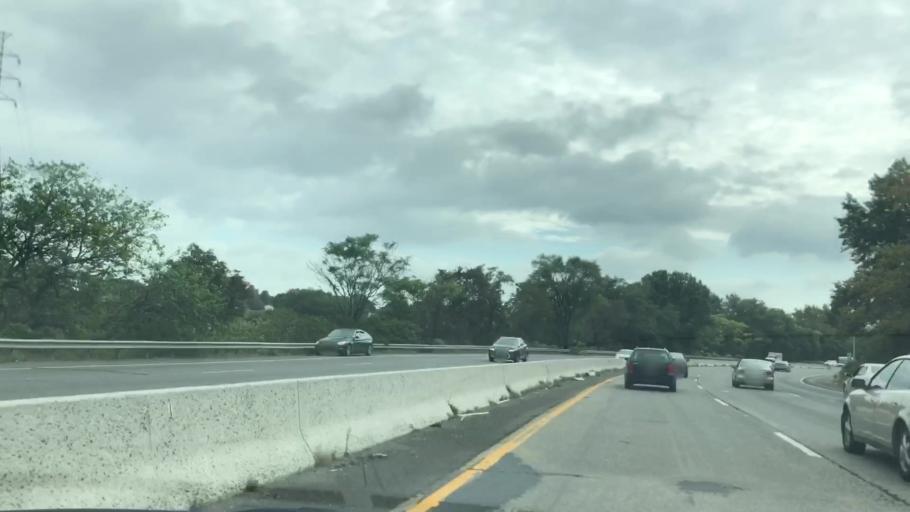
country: US
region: New Jersey
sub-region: Essex County
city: Belleville
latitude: 40.8009
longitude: -74.1395
